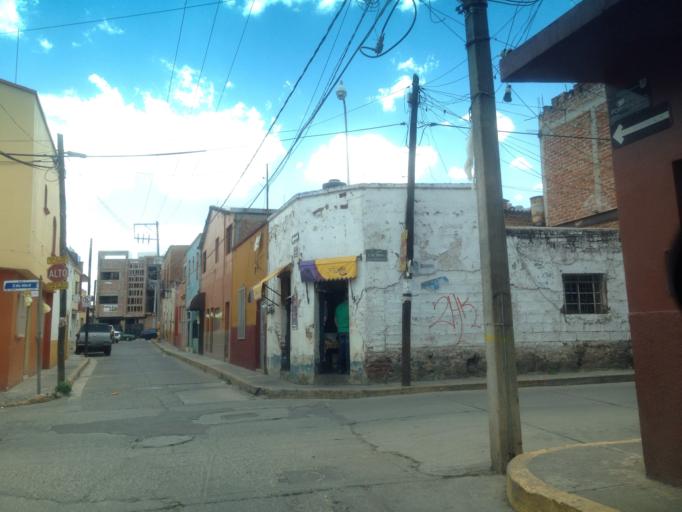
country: MX
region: Jalisco
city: Atotonilco el Alto
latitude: 20.5534
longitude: -102.5055
